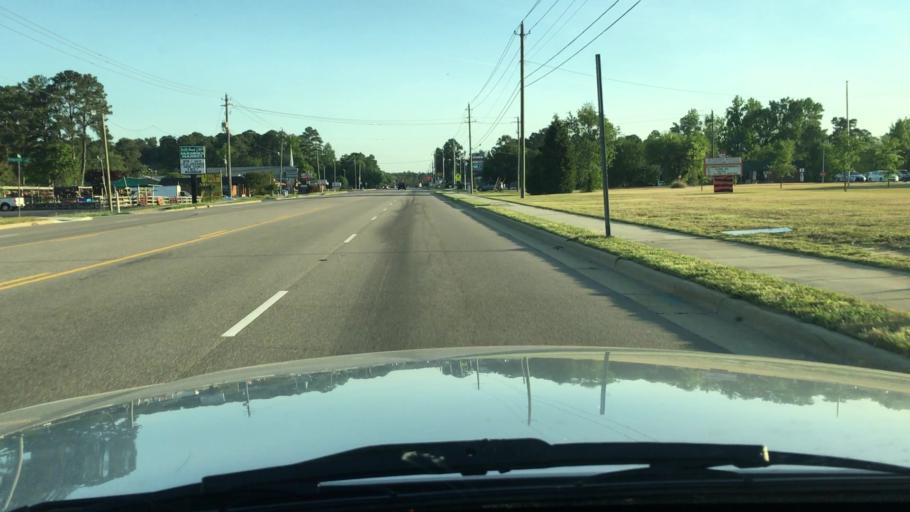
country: US
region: North Carolina
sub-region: Cumberland County
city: Fort Bragg
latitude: 35.0926
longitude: -79.0107
